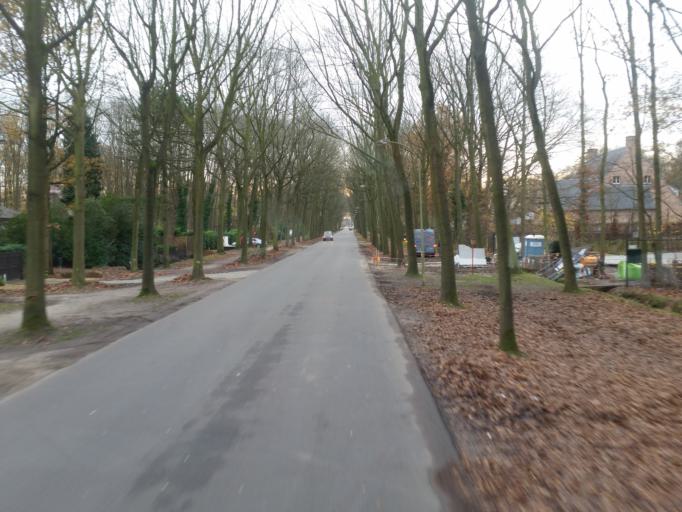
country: BE
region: Flanders
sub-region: Provincie Antwerpen
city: Brasschaat
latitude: 51.3131
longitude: 4.5016
